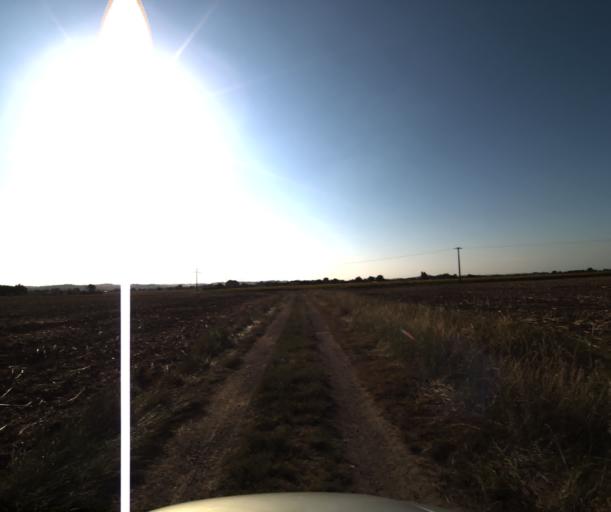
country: FR
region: Midi-Pyrenees
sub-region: Departement de la Haute-Garonne
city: Labarthe-sur-Leze
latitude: 43.4524
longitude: 1.3737
